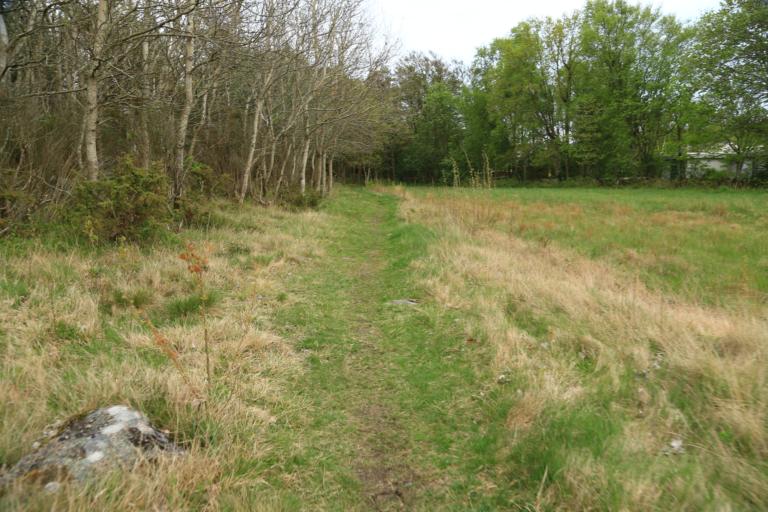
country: SE
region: Halland
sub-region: Varbergs Kommun
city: Varberg
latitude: 57.1528
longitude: 12.2293
